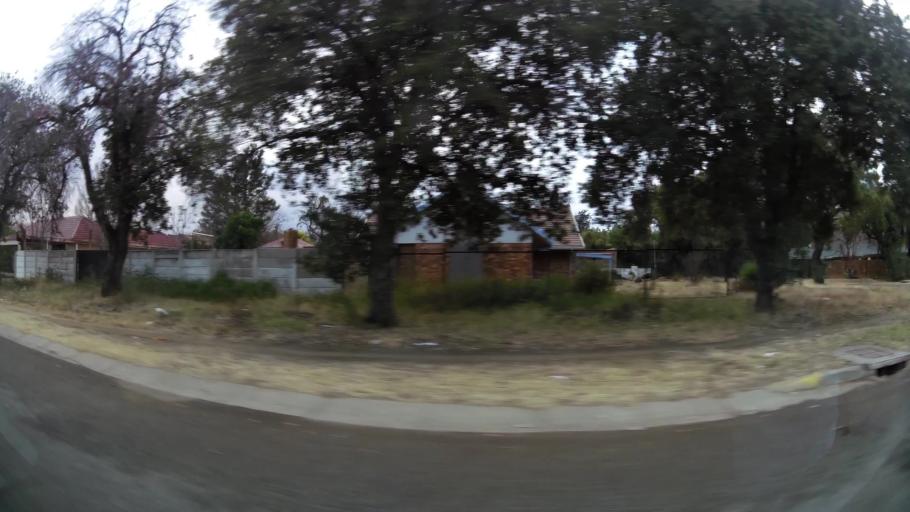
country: ZA
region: Orange Free State
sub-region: Lejweleputswa District Municipality
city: Welkom
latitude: -27.9589
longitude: 26.7371
